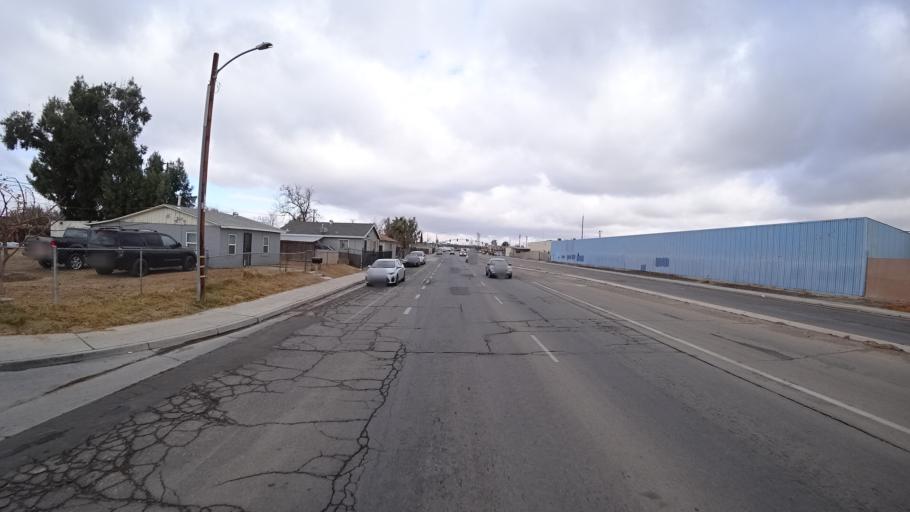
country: US
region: California
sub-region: Kern County
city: Bakersfield
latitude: 35.3487
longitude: -118.9855
